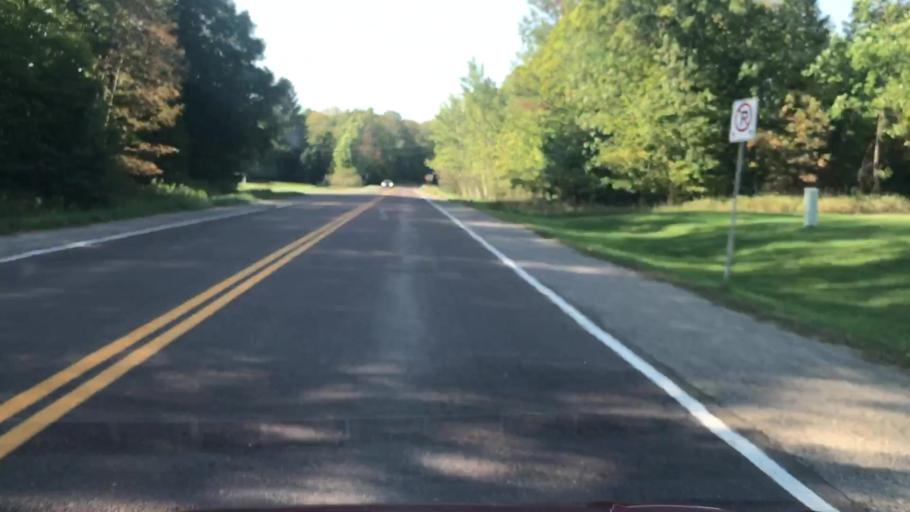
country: US
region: Michigan
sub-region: Chippewa County
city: Sault Ste. Marie
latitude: 46.2788
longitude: -84.0303
